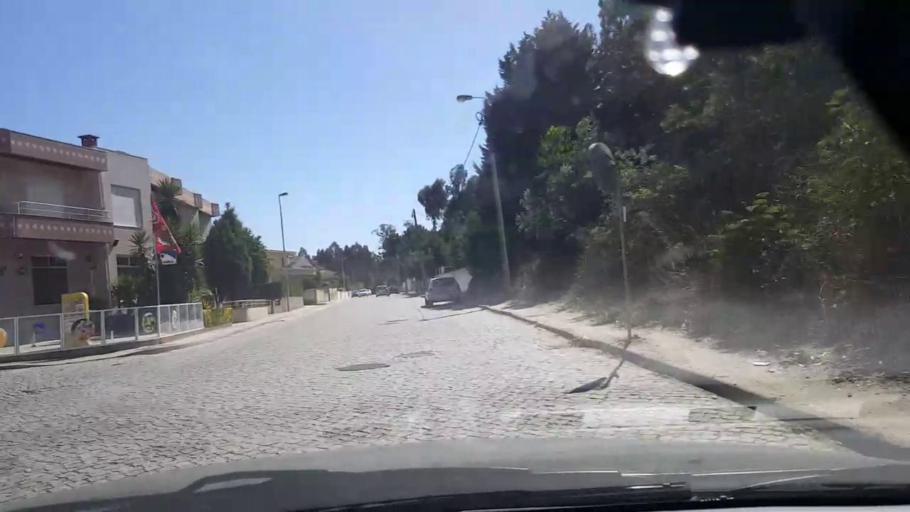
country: PT
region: Porto
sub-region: Vila do Conde
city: Arvore
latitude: 41.3308
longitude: -8.7299
